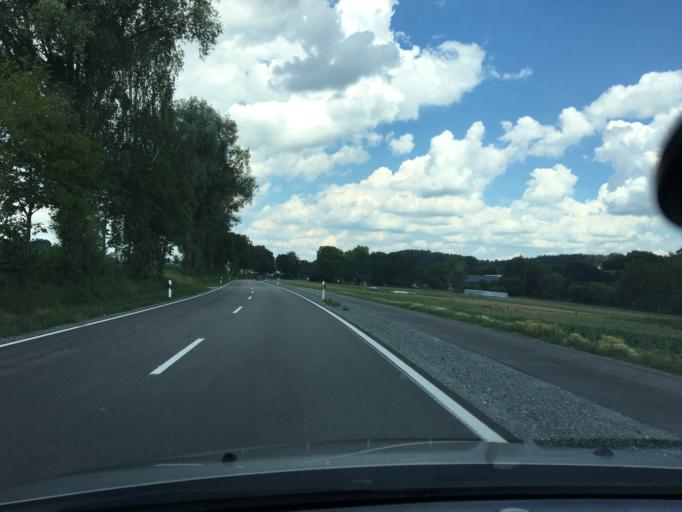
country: DE
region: Bavaria
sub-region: Upper Bavaria
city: Rohrbach
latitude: 48.2976
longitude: 12.5636
